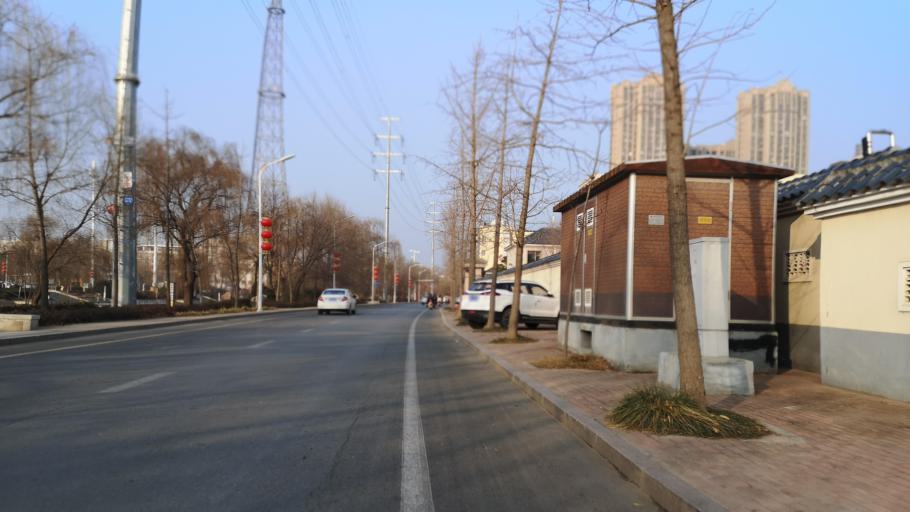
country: CN
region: Henan Sheng
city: Zhongyuanlu
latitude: 35.7777
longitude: 115.0488
